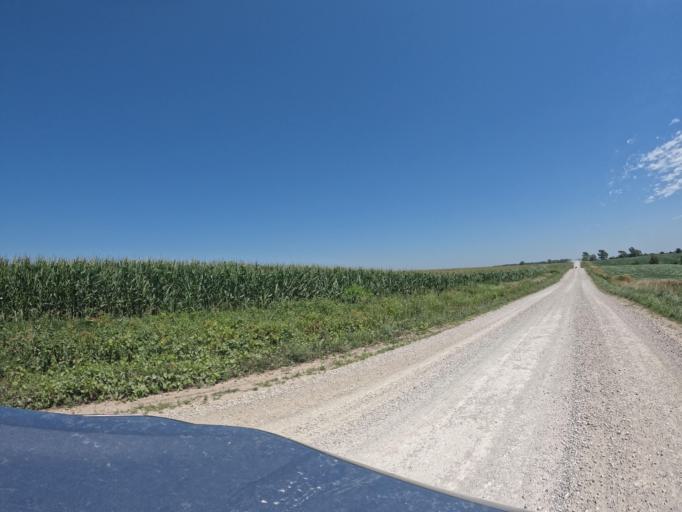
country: US
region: Iowa
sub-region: Keokuk County
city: Sigourney
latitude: 41.4525
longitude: -92.3621
